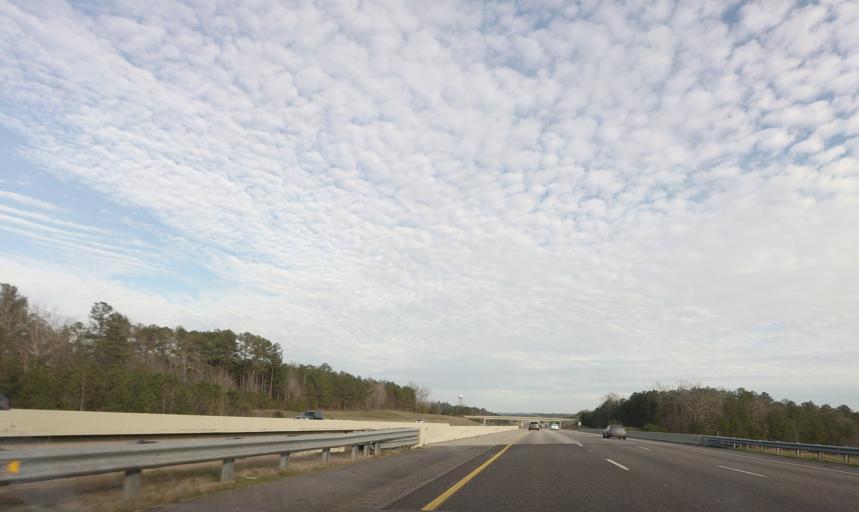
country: US
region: Alabama
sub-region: Walker County
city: Dora
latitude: 33.6651
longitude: -87.0625
